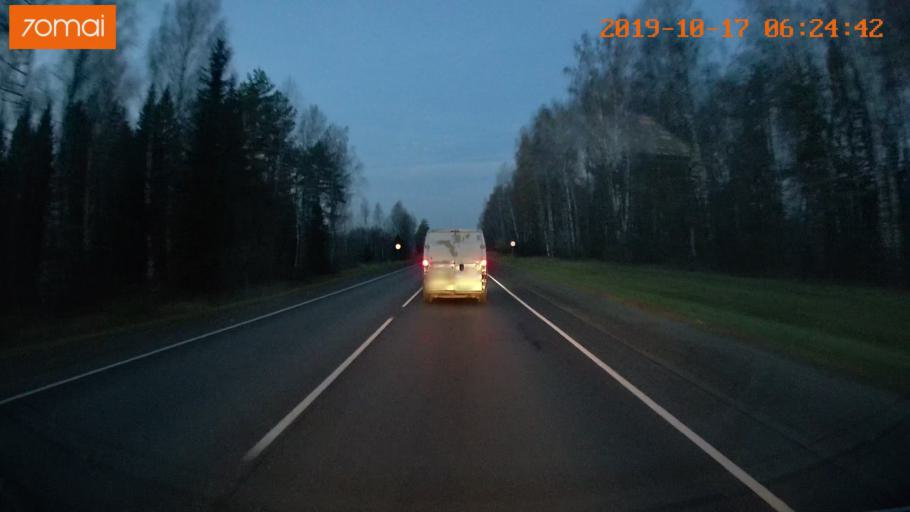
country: RU
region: Ivanovo
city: Lezhnevo
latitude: 56.7738
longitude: 40.8219
